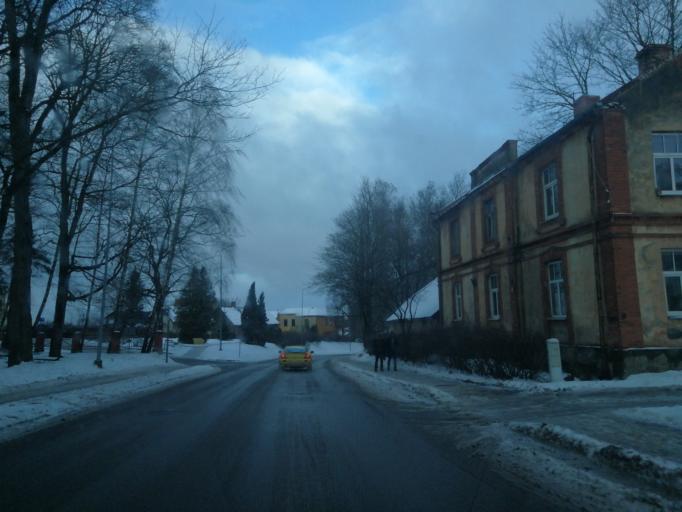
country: LV
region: Cesu Rajons
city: Cesis
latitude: 57.3066
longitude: 25.2667
